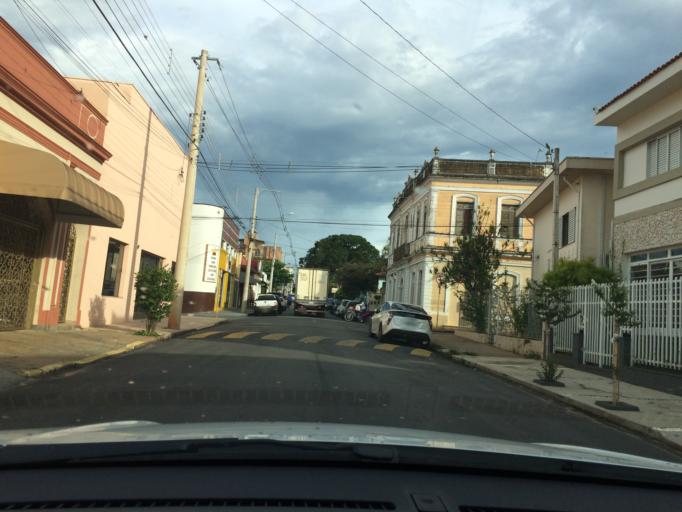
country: BR
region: Sao Paulo
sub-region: Casa Branca
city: Casa Branca
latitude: -21.7711
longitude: -47.0866
